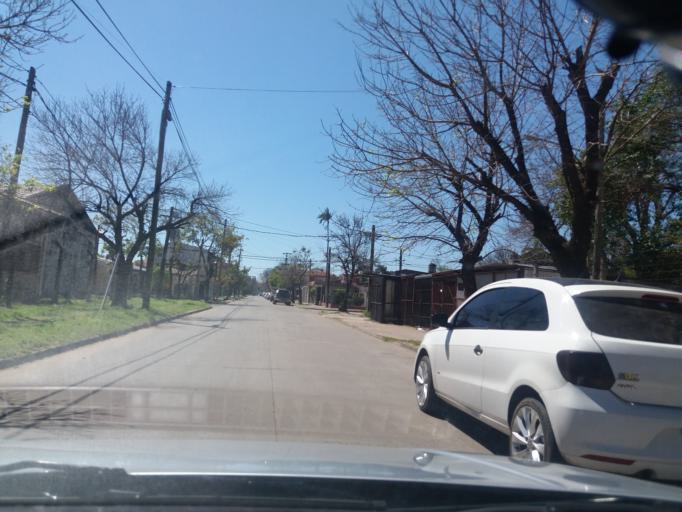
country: AR
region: Corrientes
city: Corrientes
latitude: -27.4877
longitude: -58.8447
